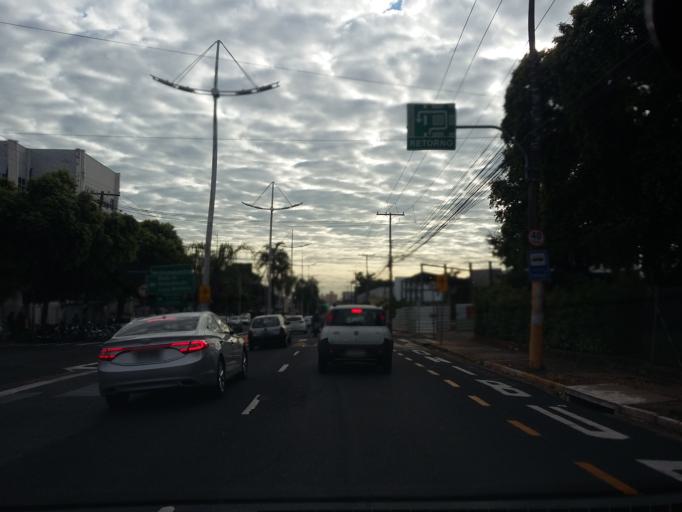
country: BR
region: Sao Paulo
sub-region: Sao Jose Do Rio Preto
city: Sao Jose do Rio Preto
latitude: -20.8298
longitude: -49.3974
